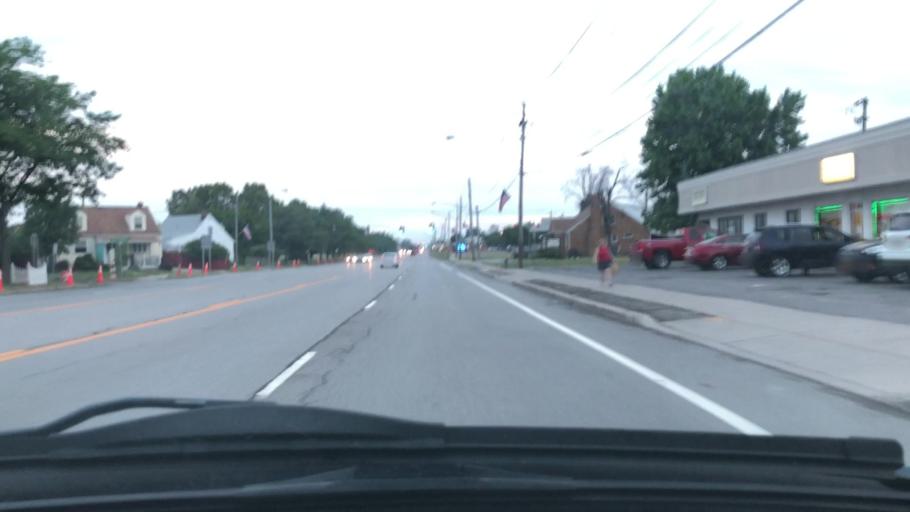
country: US
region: New York
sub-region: Erie County
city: Sloan
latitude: 42.9120
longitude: -78.7842
